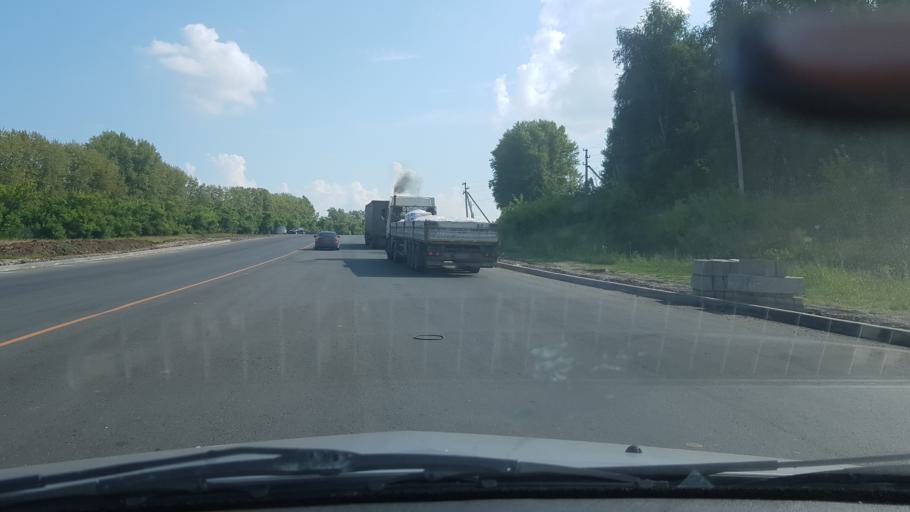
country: RU
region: Chuvashia
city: Tsivil'sk
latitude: 55.7308
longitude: 47.4478
